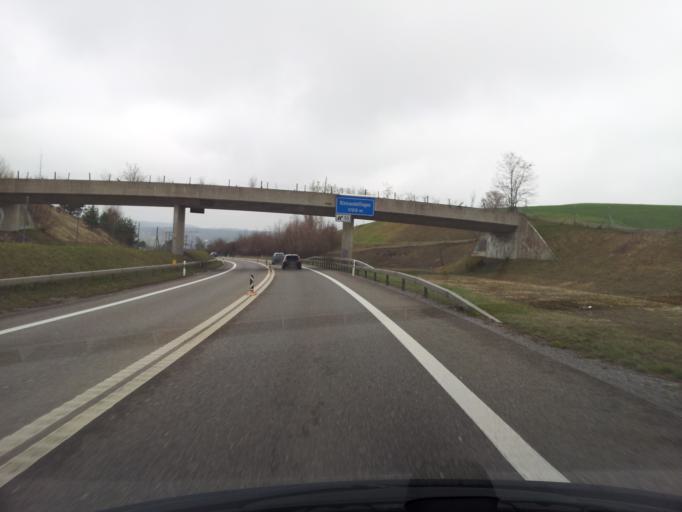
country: CH
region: Zurich
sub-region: Bezirk Andelfingen
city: Kleinandelfingen
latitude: 47.5894
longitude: 8.6905
